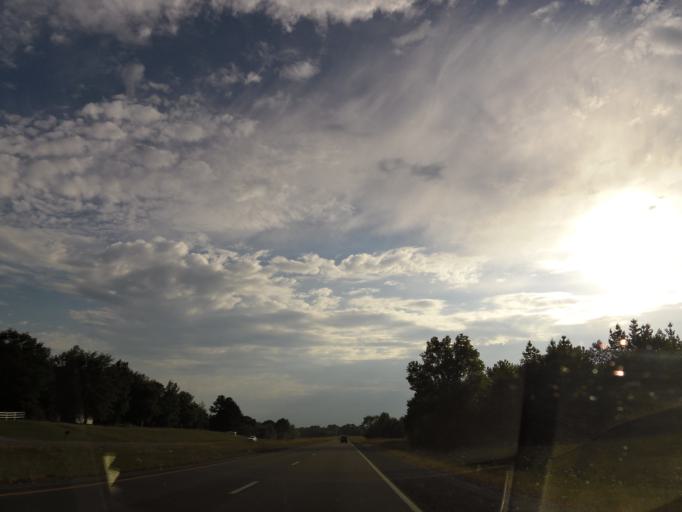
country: US
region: Alabama
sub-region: Morgan County
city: Trinity
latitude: 34.5358
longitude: -87.1670
